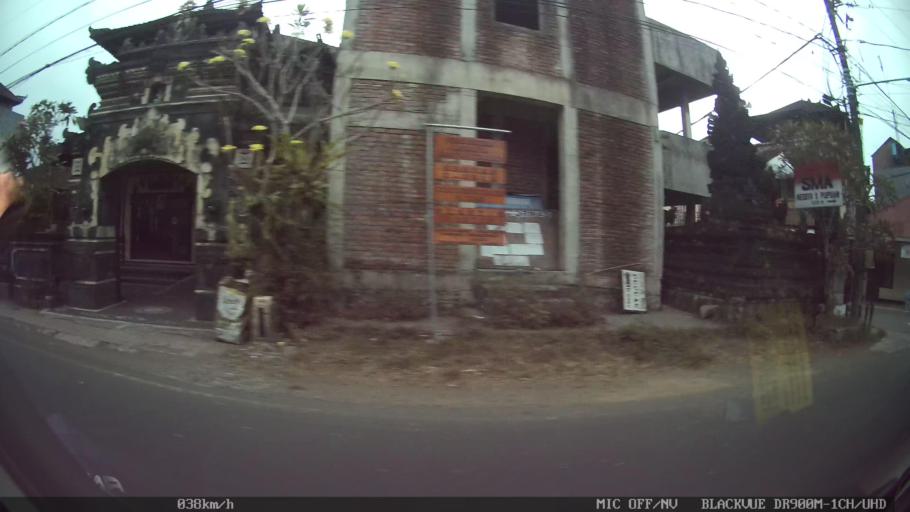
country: ID
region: Bali
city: Klau
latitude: -8.3279
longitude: 115.0297
